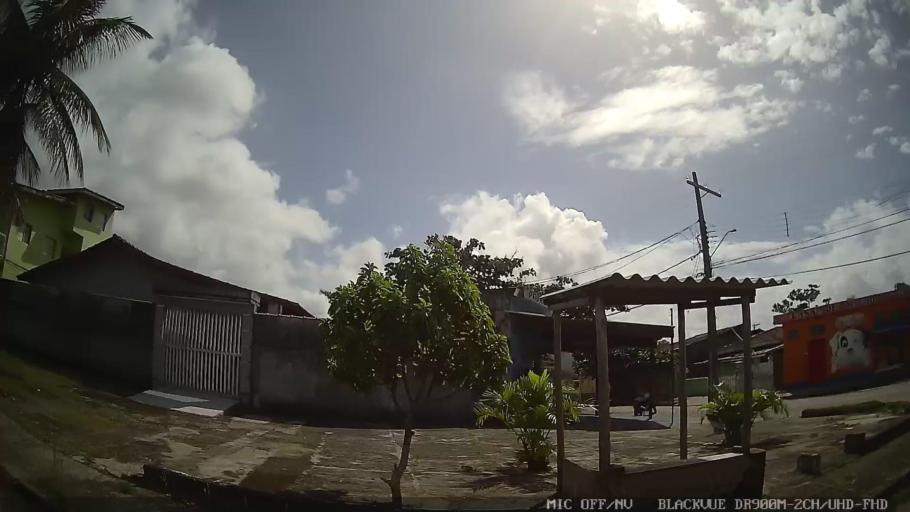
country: BR
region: Sao Paulo
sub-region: Itanhaem
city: Itanhaem
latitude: -24.1530
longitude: -46.7316
